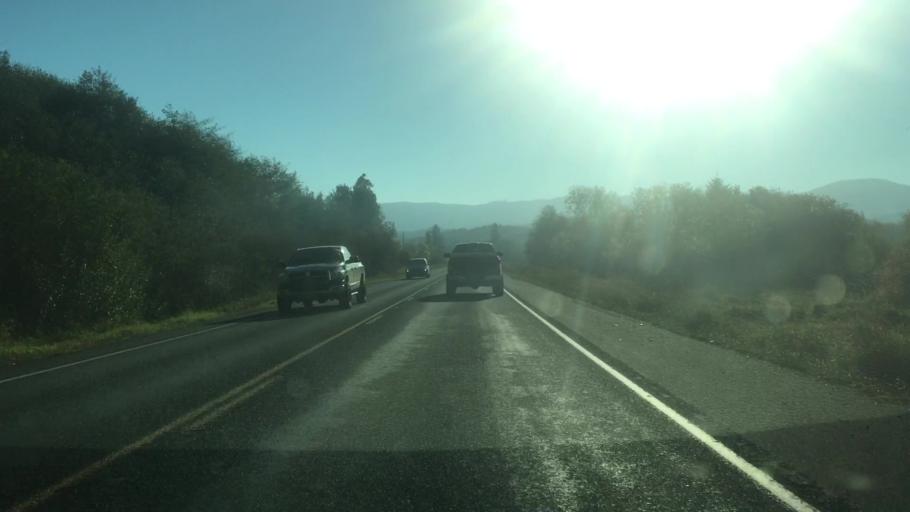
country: US
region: Oregon
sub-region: Clatsop County
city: Astoria
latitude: 46.3731
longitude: -123.8041
